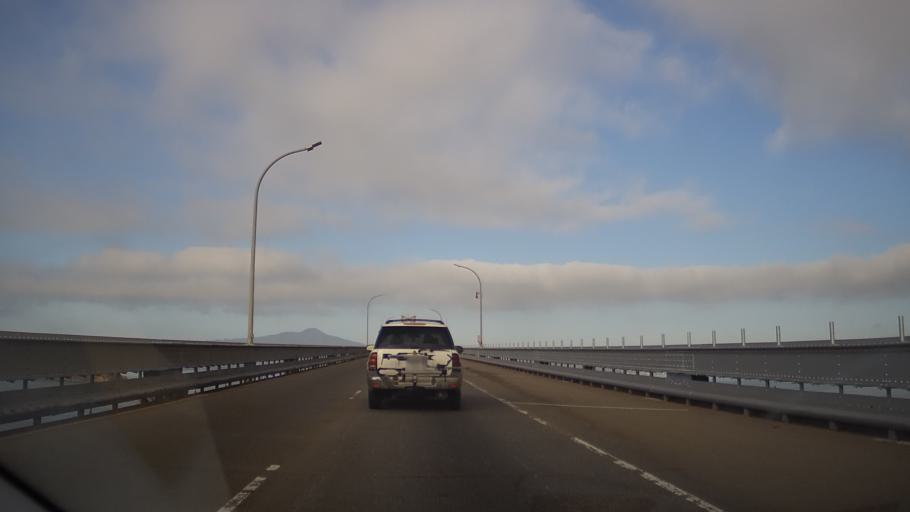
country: US
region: California
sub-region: Contra Costa County
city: North Richmond
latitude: 37.9330
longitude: -122.4165
